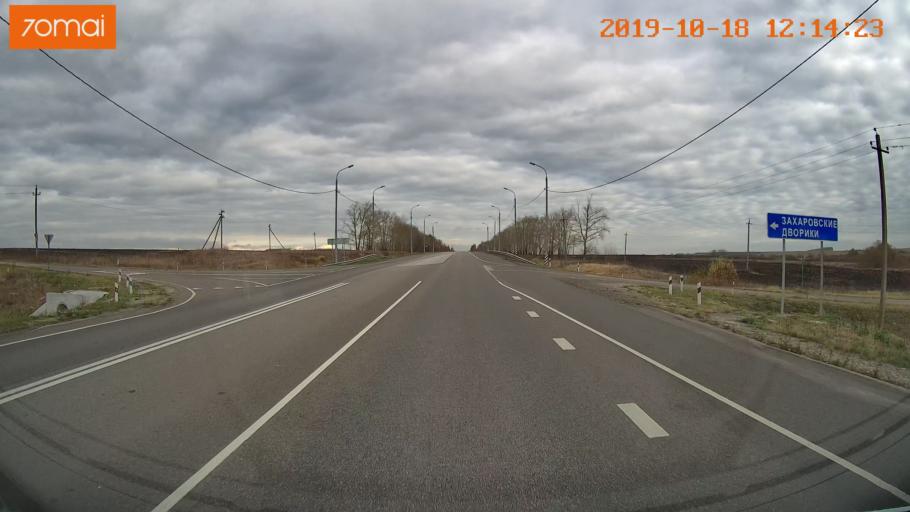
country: RU
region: Rjazan
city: Zakharovo
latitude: 54.4302
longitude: 39.3824
